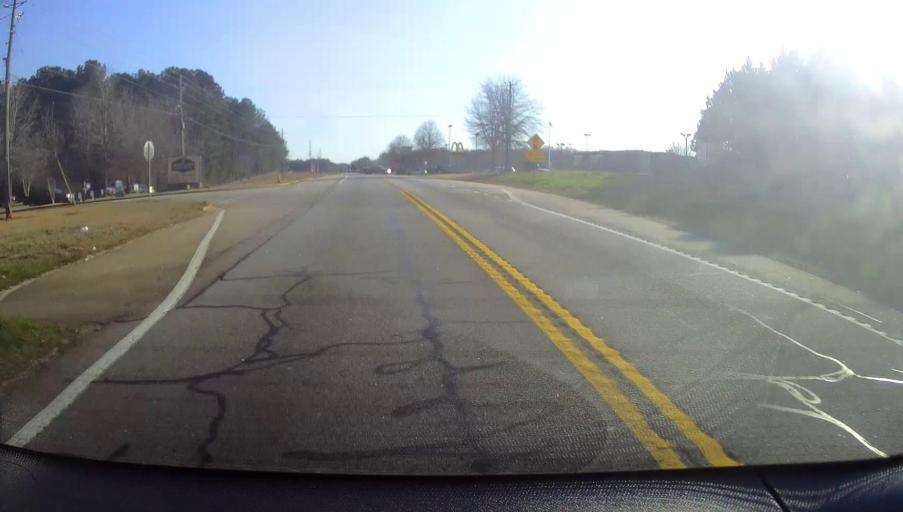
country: US
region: Georgia
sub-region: Henry County
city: Locust Grove
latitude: 33.3677
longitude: -84.1796
